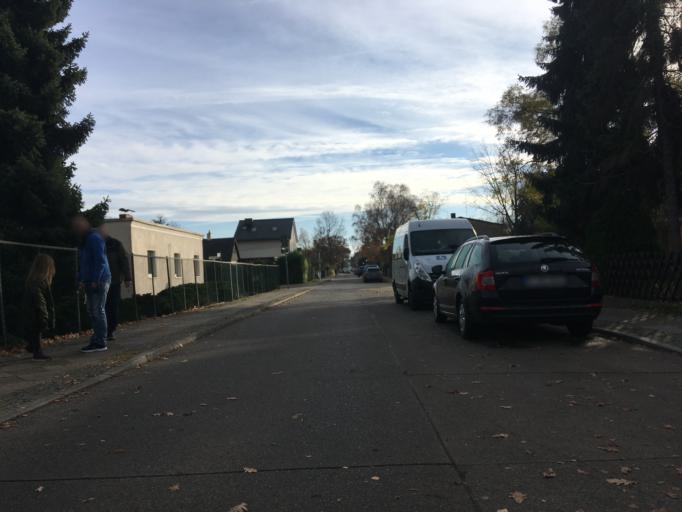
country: DE
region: Berlin
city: Rudow
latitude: 52.4370
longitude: 13.4785
